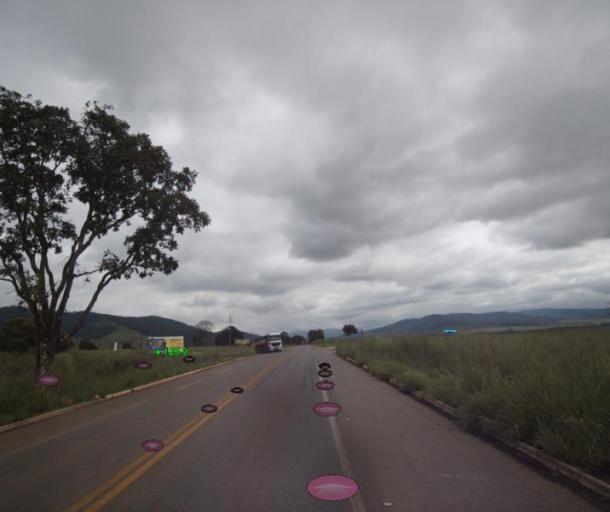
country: BR
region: Goias
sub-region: Barro Alto
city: Barro Alto
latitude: -15.0244
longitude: -48.8960
